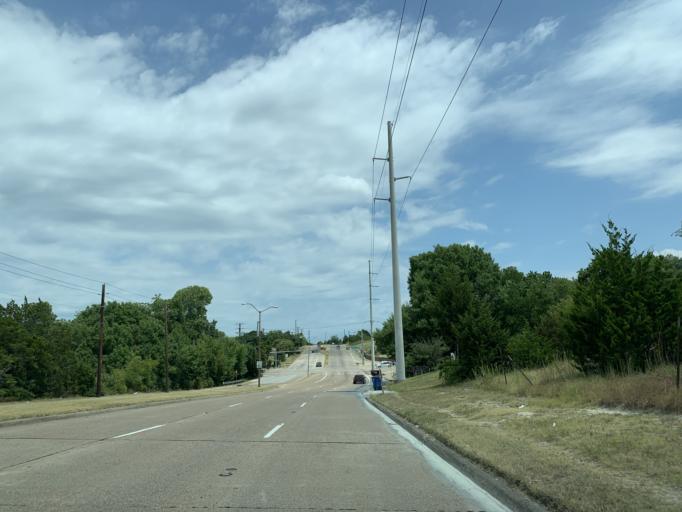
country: US
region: Texas
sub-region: Dallas County
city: Lancaster
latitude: 32.6623
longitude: -96.8075
